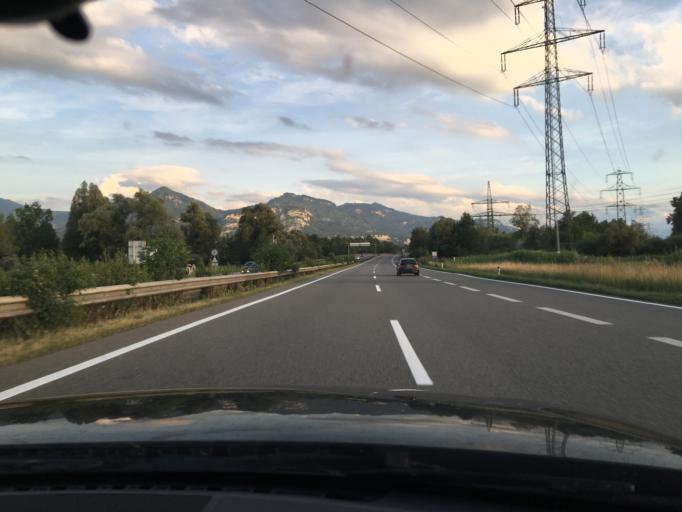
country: AT
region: Vorarlberg
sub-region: Politischer Bezirk Dornbirn
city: Dornbirn
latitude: 47.4440
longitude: 9.7230
